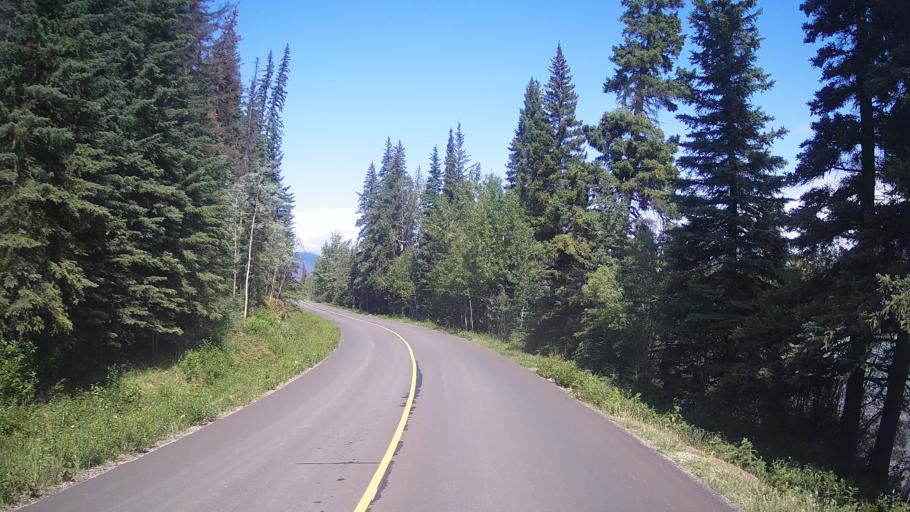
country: CA
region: Alberta
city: Jasper Park Lodge
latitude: 52.7385
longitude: -117.9586
